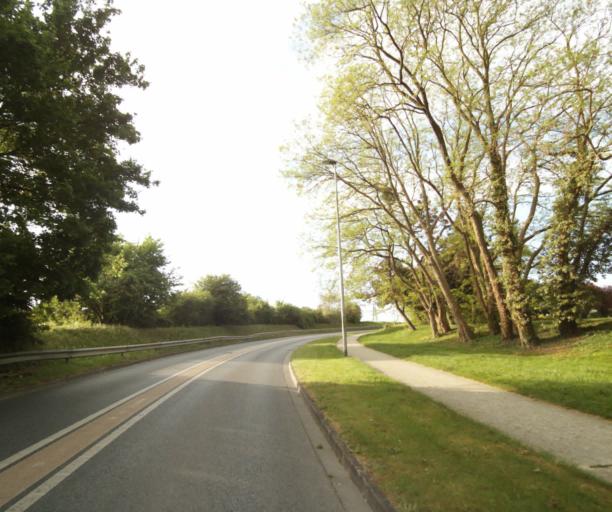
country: FR
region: Ile-de-France
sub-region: Departement de Seine-et-Marne
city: Torcy
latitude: 48.8546
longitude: 2.6593
